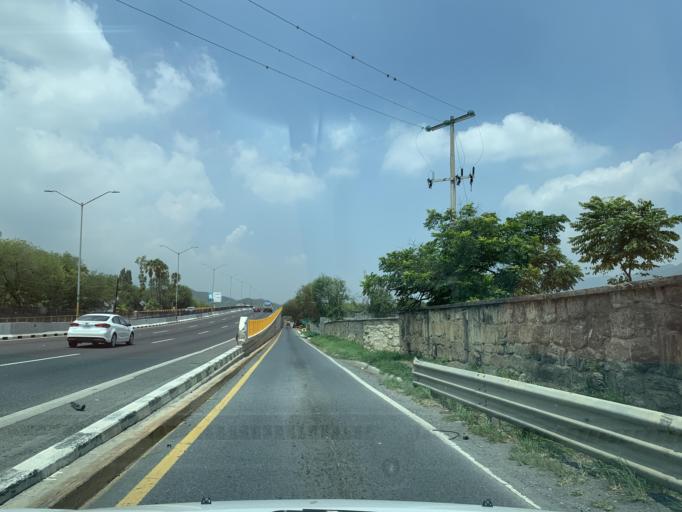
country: MX
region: Nuevo Leon
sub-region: Juarez
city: Bosques de San Pedro
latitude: 25.5218
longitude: -100.2041
